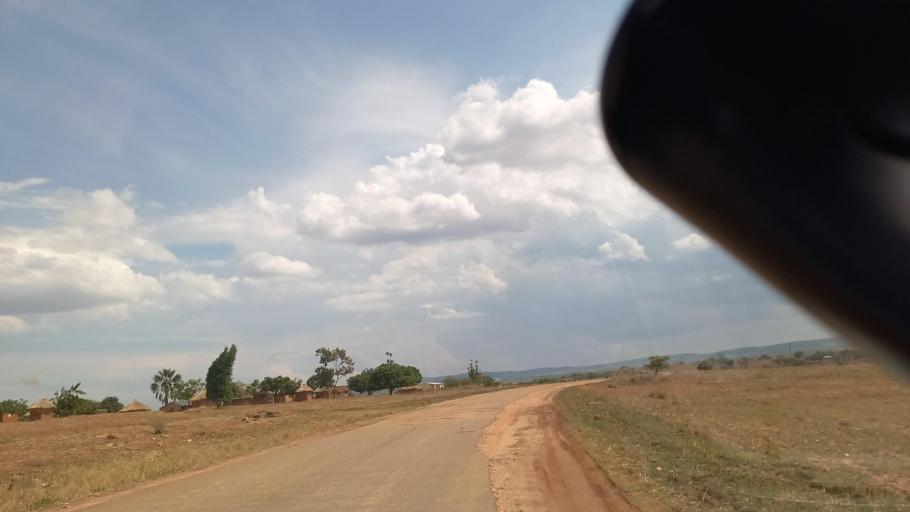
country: ZM
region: Lusaka
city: Kafue
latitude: -16.1768
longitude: 28.0889
